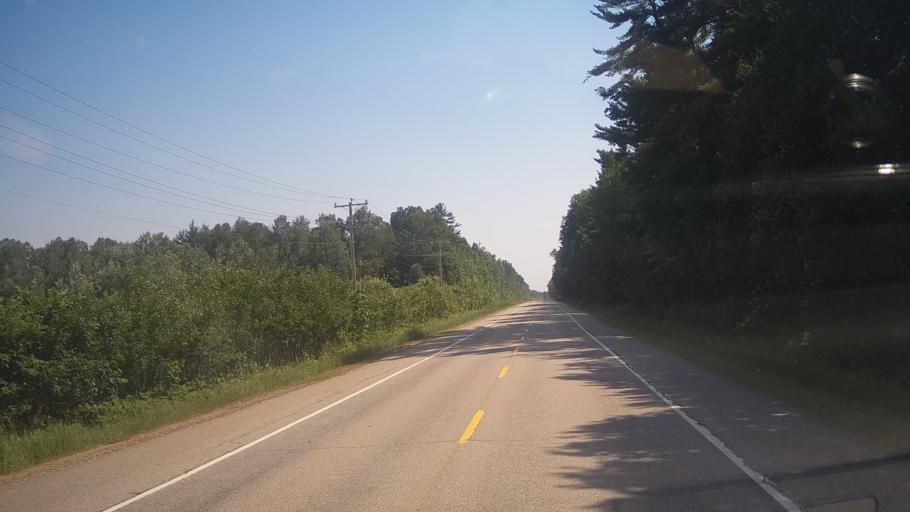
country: CA
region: Ontario
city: Pembroke
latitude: 45.8432
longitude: -77.0135
